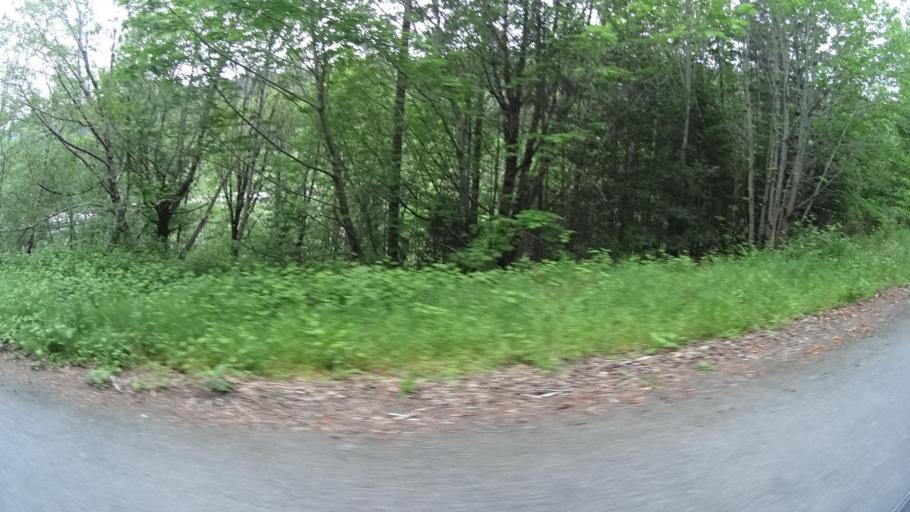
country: US
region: California
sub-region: Humboldt County
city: Willow Creek
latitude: 41.2066
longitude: -123.7577
